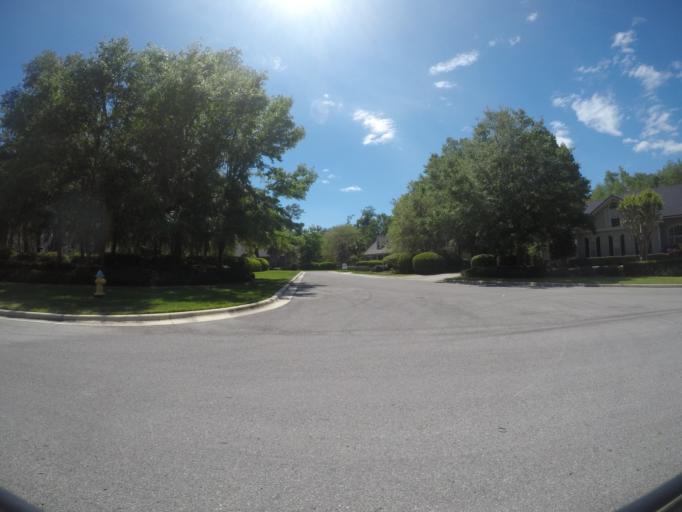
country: US
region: Florida
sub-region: Alachua County
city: Gainesville
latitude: 29.6170
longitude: -82.4375
